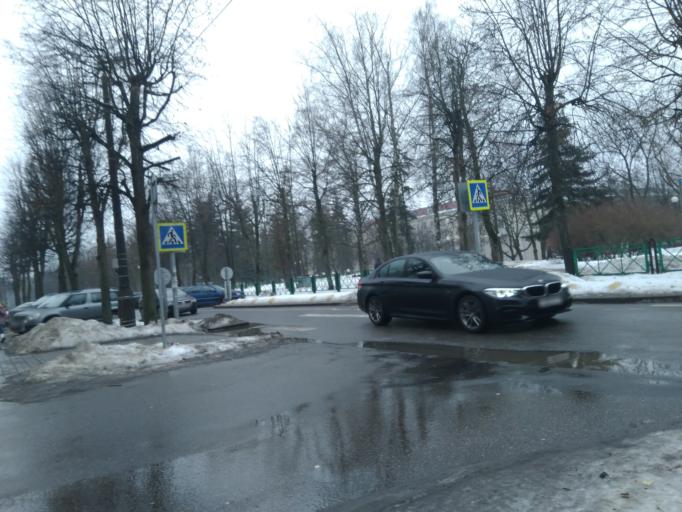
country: BY
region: Minsk
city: Minsk
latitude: 53.9277
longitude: 27.6130
